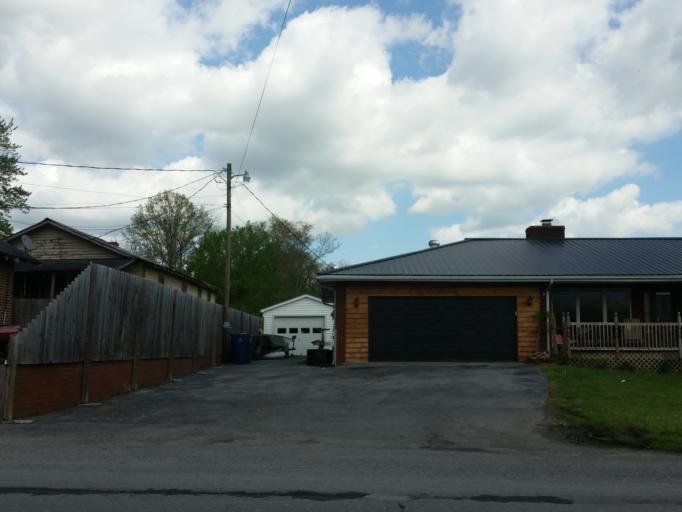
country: US
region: Kentucky
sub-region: Bell County
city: Middlesboro
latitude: 36.6295
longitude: -83.7161
